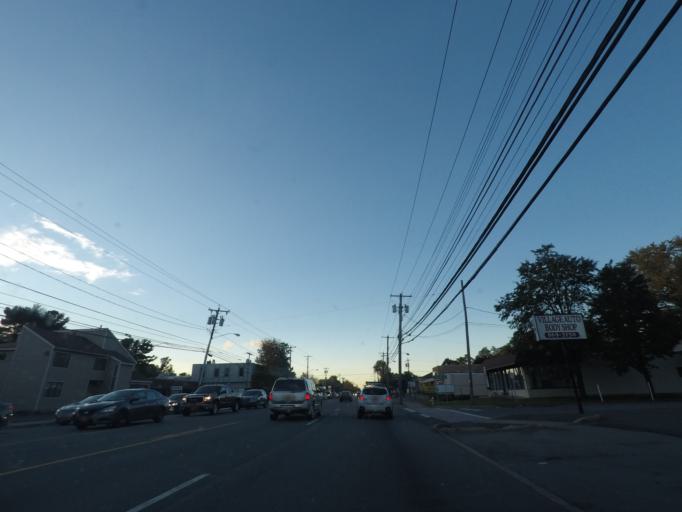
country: US
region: New York
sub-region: Albany County
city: Colonie
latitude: 42.7229
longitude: -73.8388
